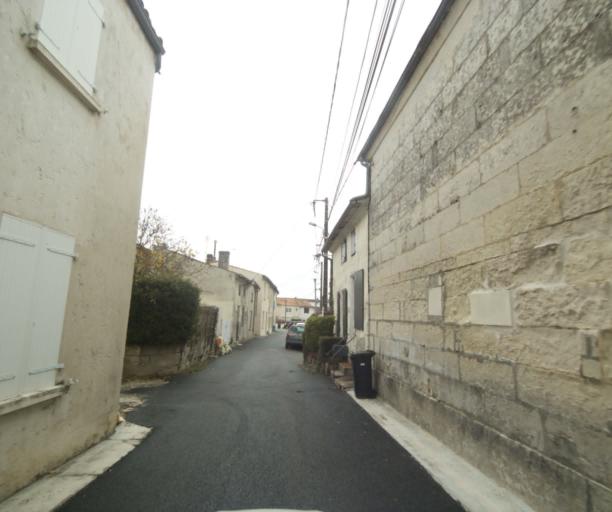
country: FR
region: Poitou-Charentes
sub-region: Departement de la Charente-Maritime
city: Saintes
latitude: 45.7264
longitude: -0.6432
